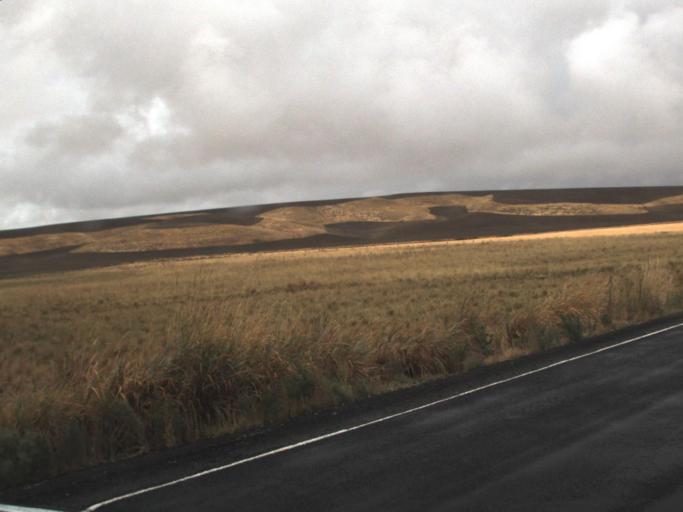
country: US
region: Washington
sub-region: Spokane County
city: Cheney
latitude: 47.1237
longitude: -117.8270
